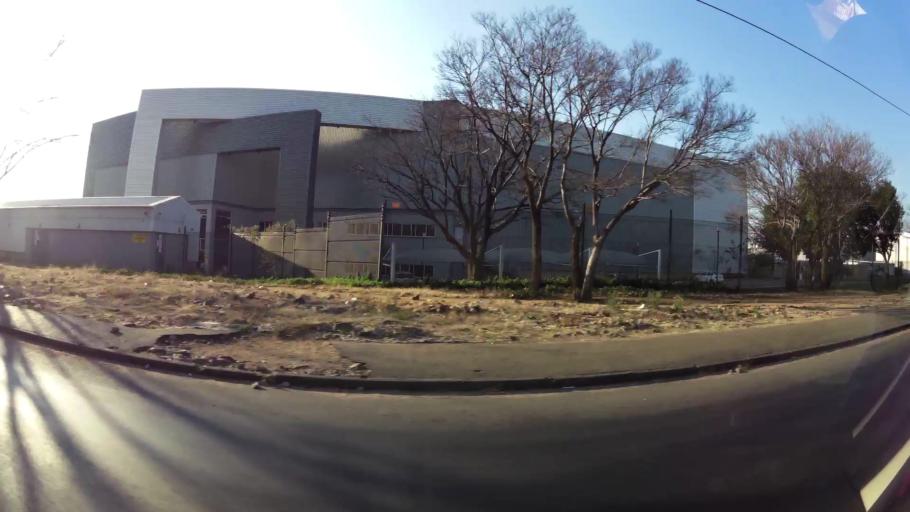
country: ZA
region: Gauteng
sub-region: Ekurhuleni Metropolitan Municipality
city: Germiston
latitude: -26.1621
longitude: 28.1969
